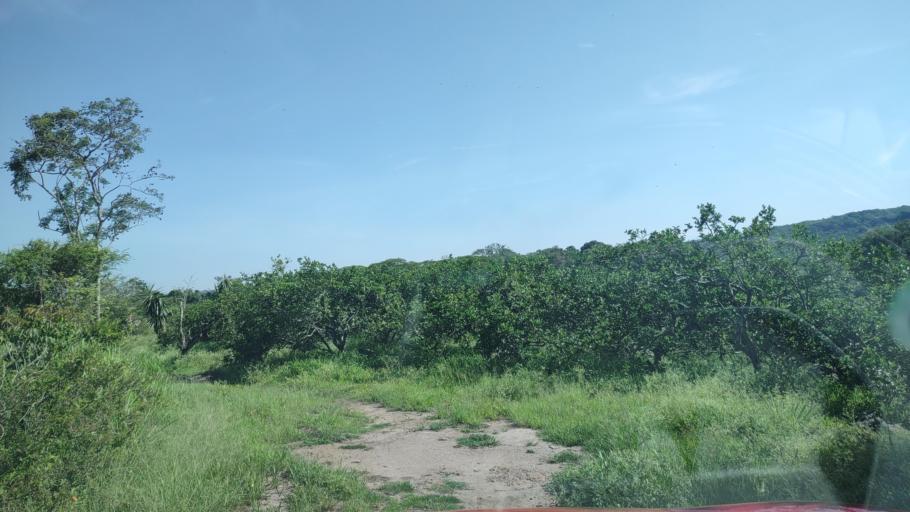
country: MX
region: Veracruz
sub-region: Emiliano Zapata
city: Dos Rios
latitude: 19.4339
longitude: -96.8017
